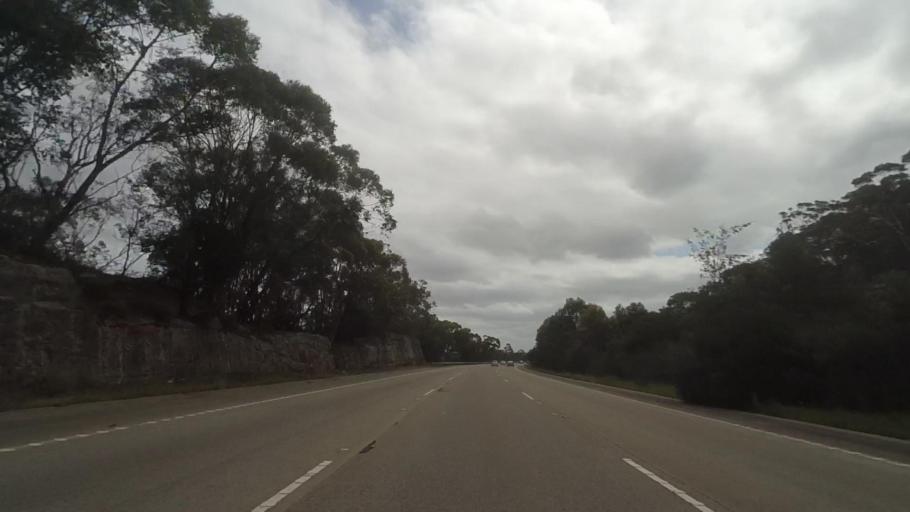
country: AU
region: New South Wales
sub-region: Gosford Shire
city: Point Clare
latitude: -33.4332
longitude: 151.2702
